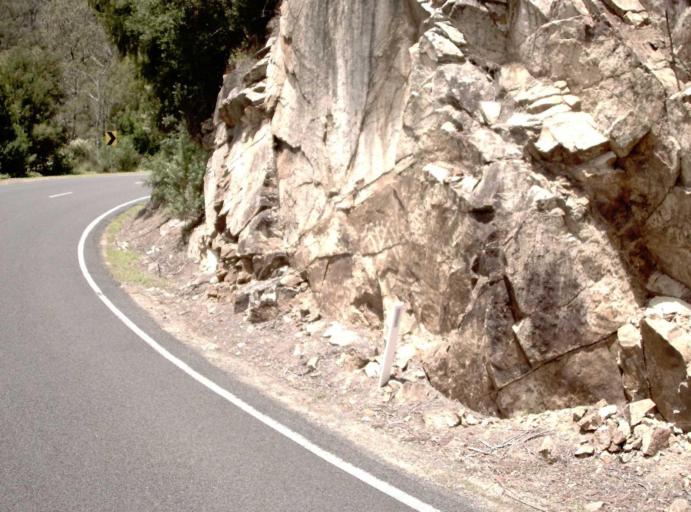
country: AU
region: Victoria
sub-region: East Gippsland
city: Lakes Entrance
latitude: -37.5501
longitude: 147.8739
